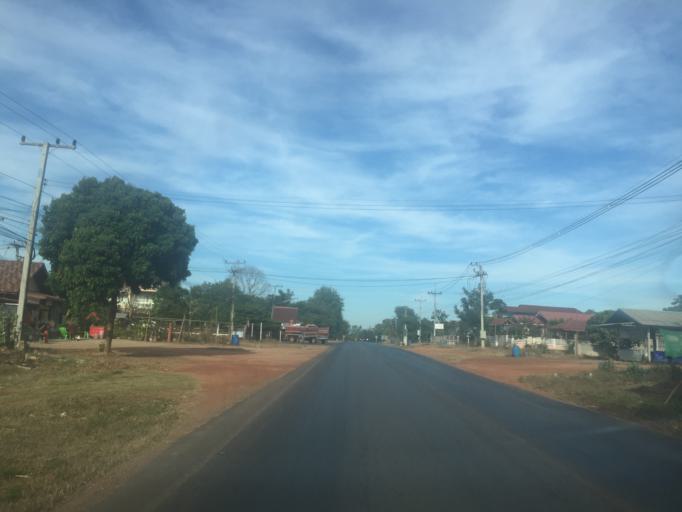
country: TH
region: Changwat Udon Thani
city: Si That
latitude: 16.9825
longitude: 103.1834
